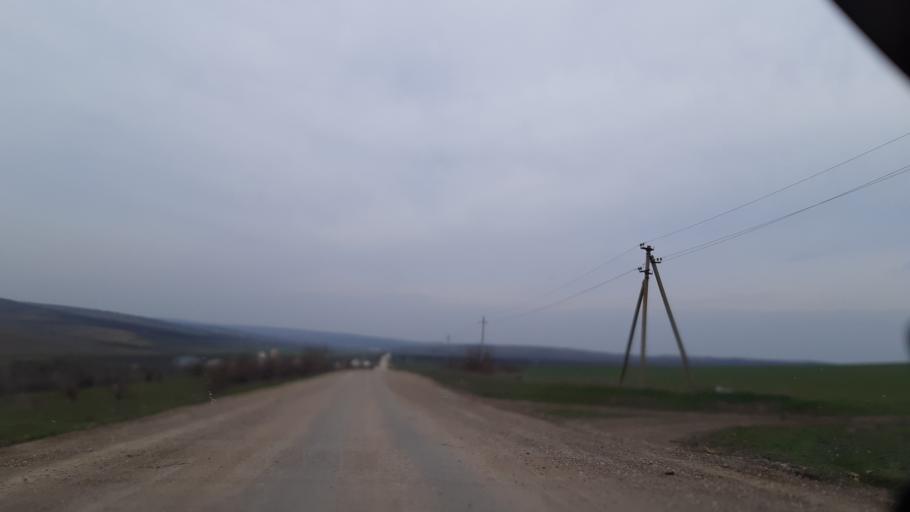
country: MD
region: Soldanesti
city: Soldanesti
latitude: 47.5958
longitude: 28.6496
